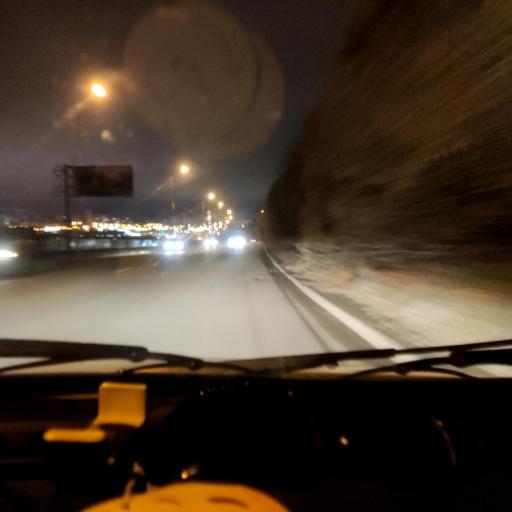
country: RU
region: Bashkortostan
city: Ufa
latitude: 54.7035
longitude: 55.9679
